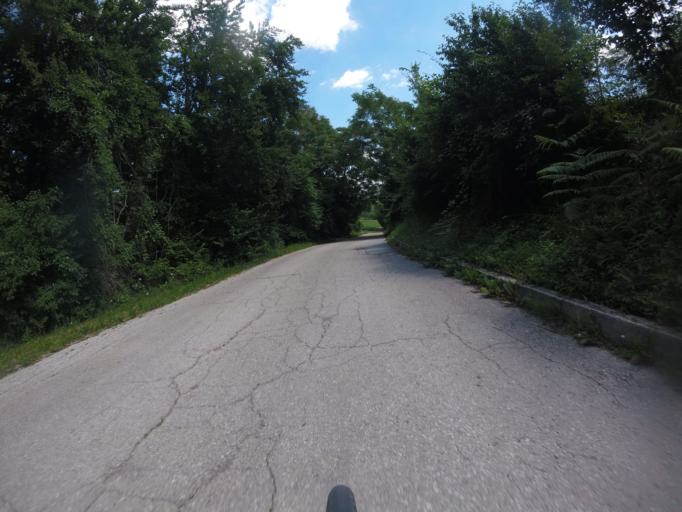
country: HR
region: Karlovacka
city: Ozalj
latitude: 45.6790
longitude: 15.4494
